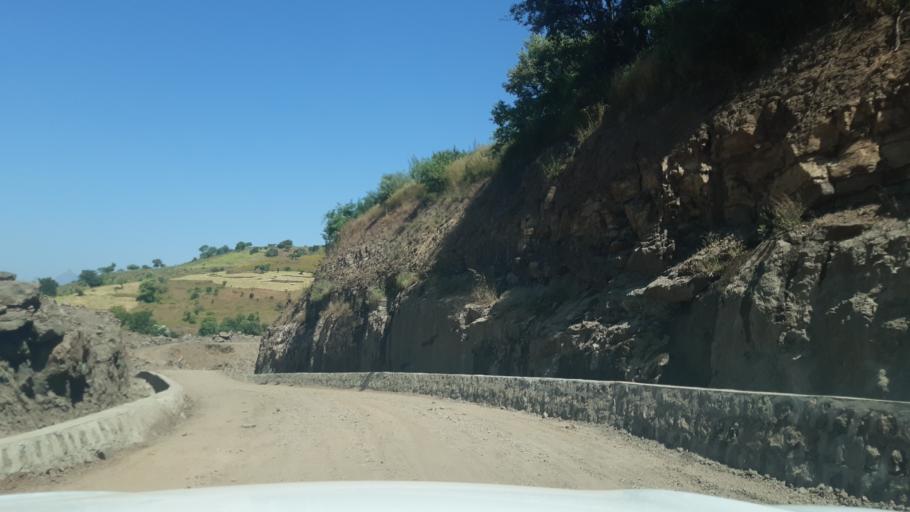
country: ET
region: Amhara
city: Dabat
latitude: 13.1671
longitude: 37.6057
